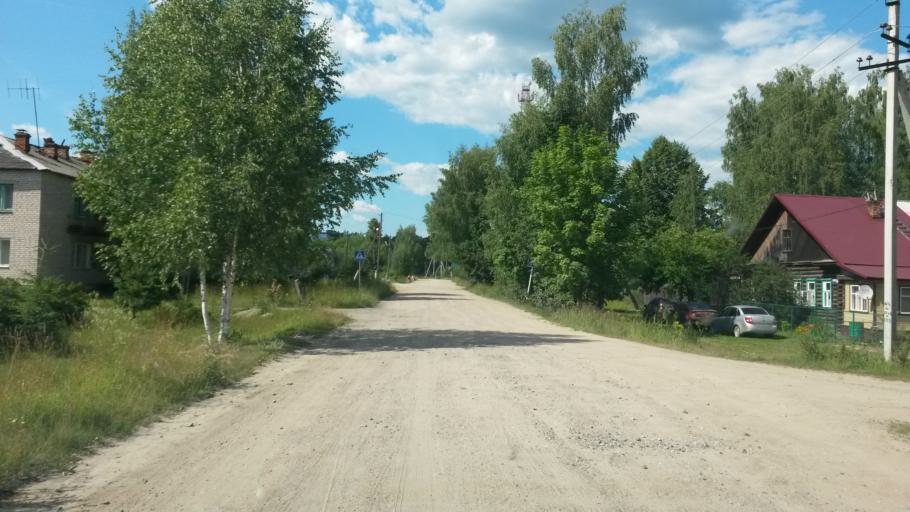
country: RU
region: Ivanovo
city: Zarechnyy
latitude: 57.4972
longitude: 42.3338
